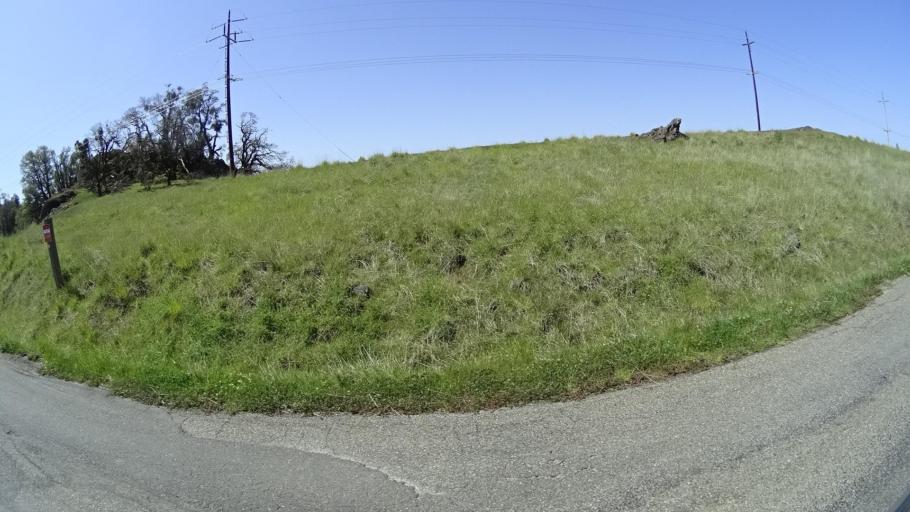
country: US
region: California
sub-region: Humboldt County
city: Redway
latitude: 40.0966
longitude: -123.6818
